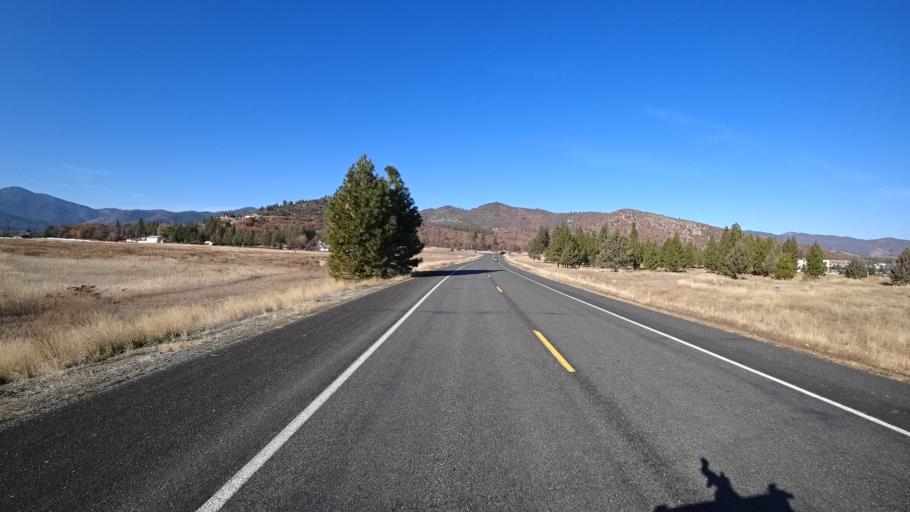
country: US
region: California
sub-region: Siskiyou County
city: Yreka
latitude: 41.6960
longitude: -122.6453
